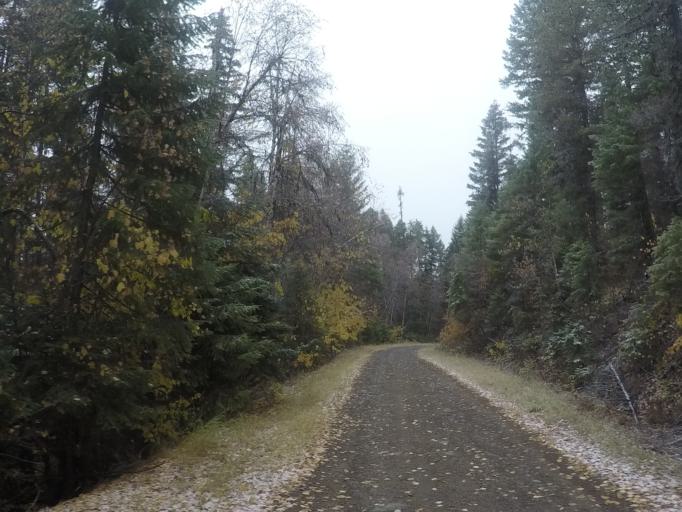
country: US
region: Montana
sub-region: Flathead County
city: Bigfork
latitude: 47.8826
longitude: -113.8756
